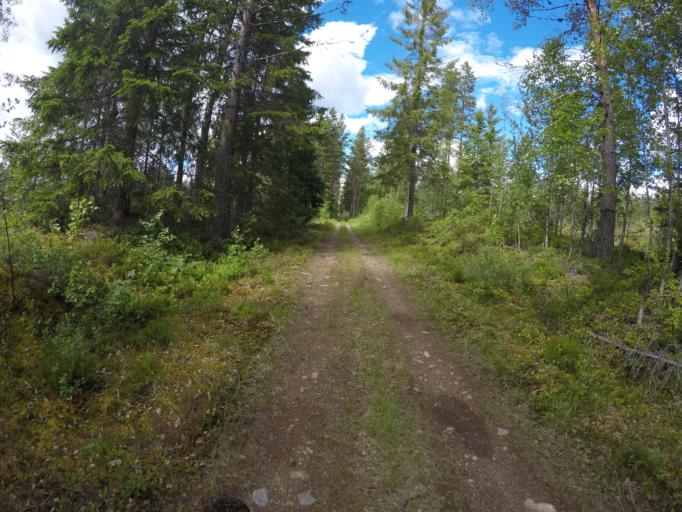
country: SE
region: Vaermland
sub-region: Filipstads Kommun
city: Lesjofors
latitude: 60.1429
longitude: 14.2481
